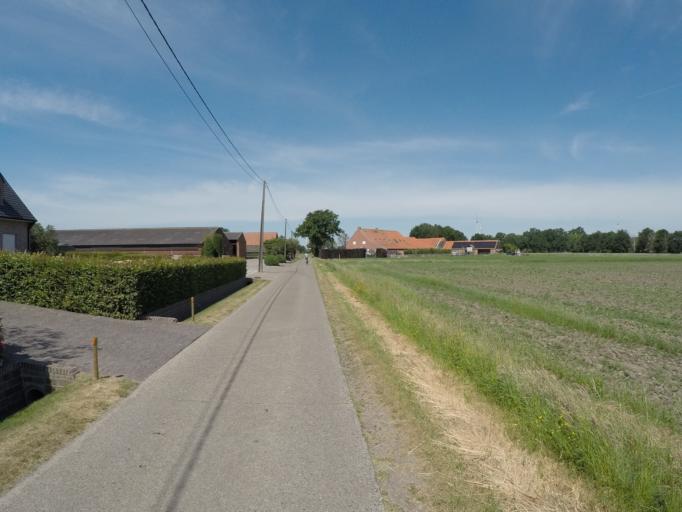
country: BE
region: Flanders
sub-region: Provincie Antwerpen
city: Brecht
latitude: 51.3654
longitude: 4.6753
